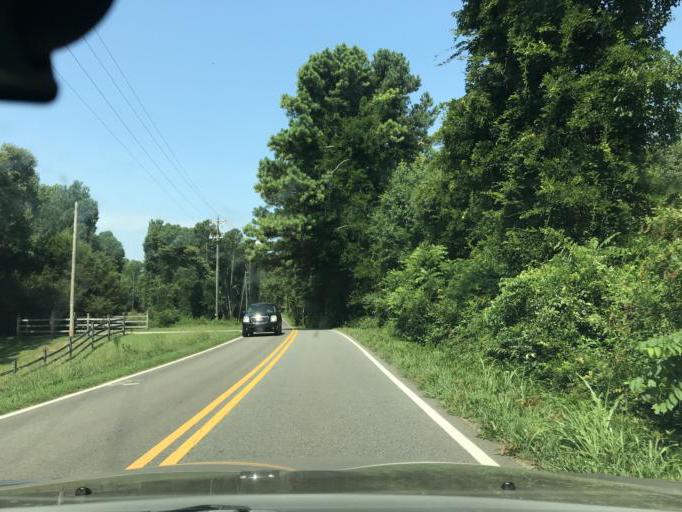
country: US
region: Georgia
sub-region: Hall County
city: Flowery Branch
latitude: 34.2321
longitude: -84.0004
